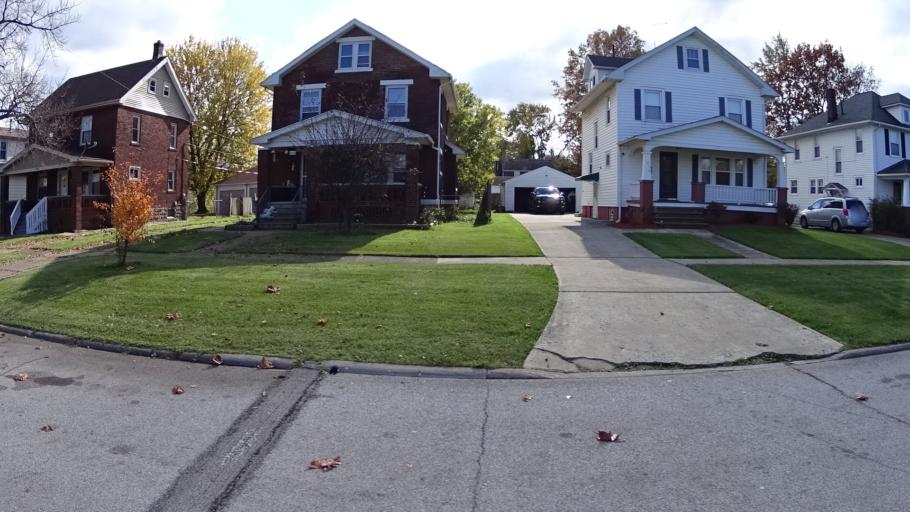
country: US
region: Ohio
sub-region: Lorain County
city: Sheffield
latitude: 41.4401
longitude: -82.1310
